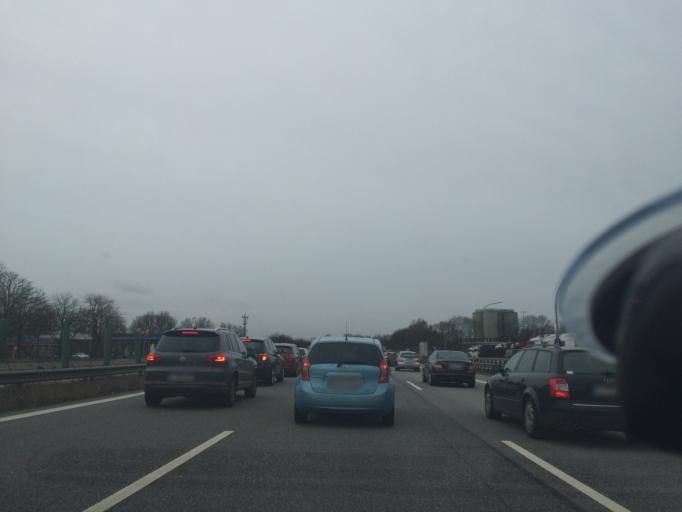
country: DE
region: Hamburg
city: Harburg
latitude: 53.4844
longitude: 10.0259
